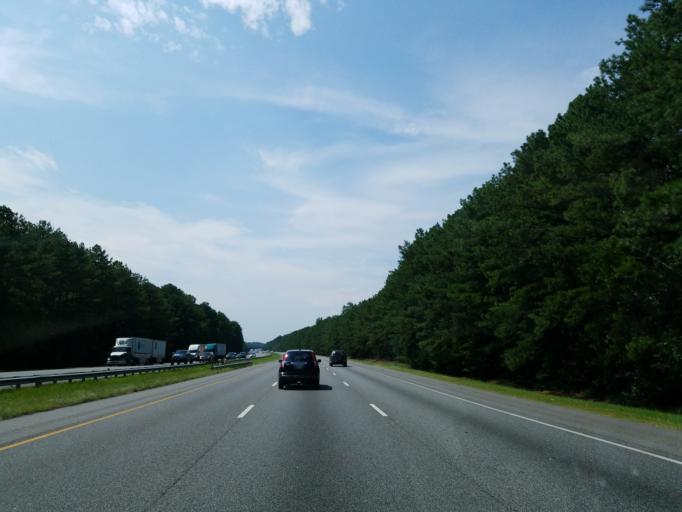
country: US
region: Georgia
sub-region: Bartow County
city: Adairsville
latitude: 34.3278
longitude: -84.8553
